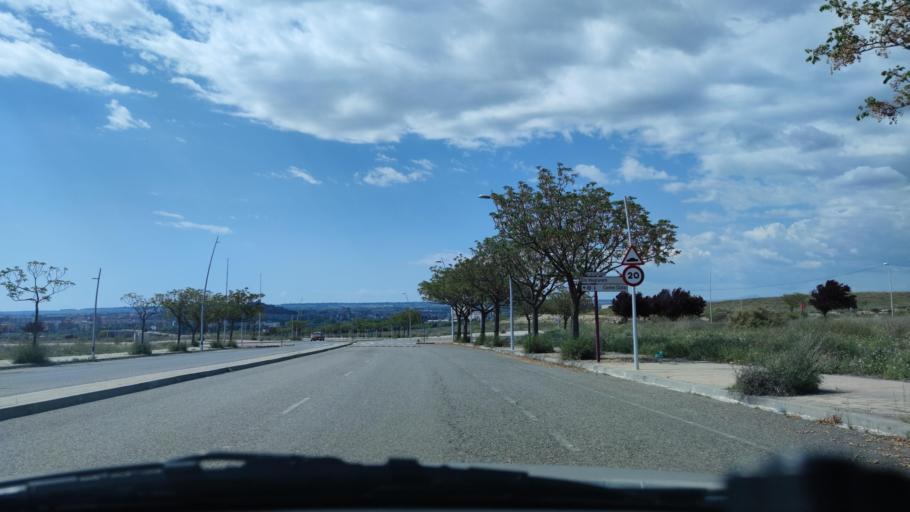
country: ES
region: Catalonia
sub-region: Provincia de Lleida
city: Lleida
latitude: 41.6041
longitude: 0.6619
